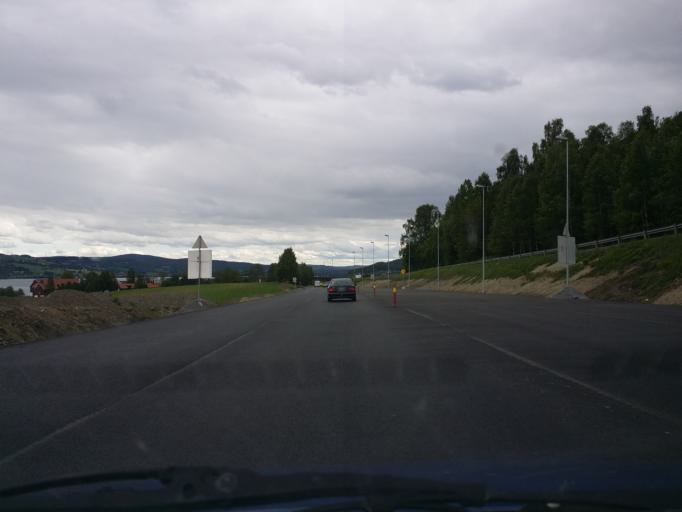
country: NO
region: Hedmark
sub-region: Ringsaker
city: Moelv
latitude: 60.9761
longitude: 10.5862
